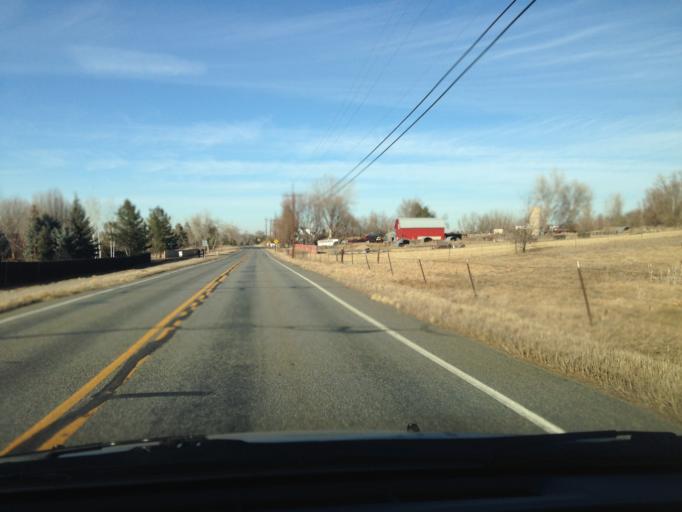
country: US
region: Colorado
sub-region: Boulder County
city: Niwot
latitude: 40.0902
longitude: -105.1691
